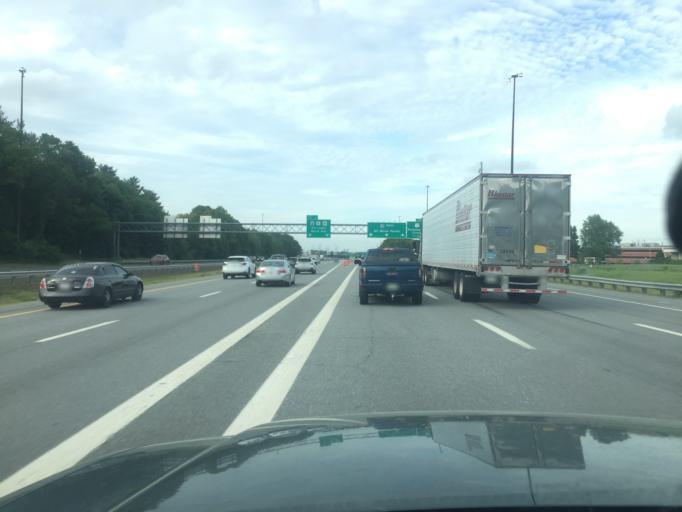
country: US
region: New Hampshire
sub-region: Rockingham County
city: Greenland
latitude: 43.0535
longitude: -70.8129
